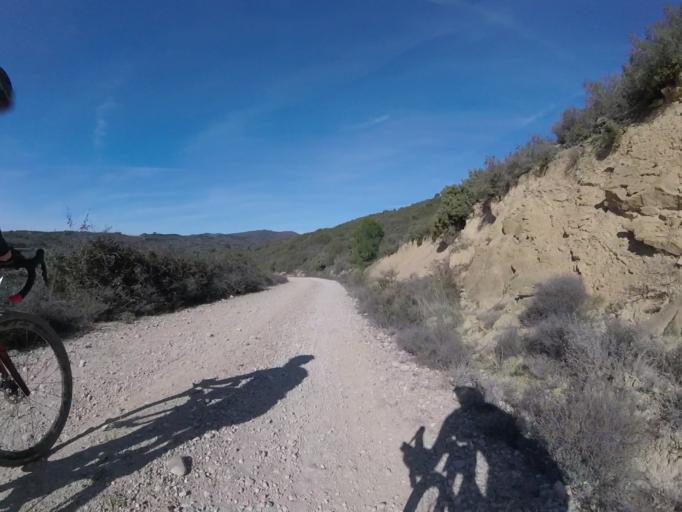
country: ES
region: Navarre
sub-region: Provincia de Navarra
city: Maneru
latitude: 42.6349
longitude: -1.8826
